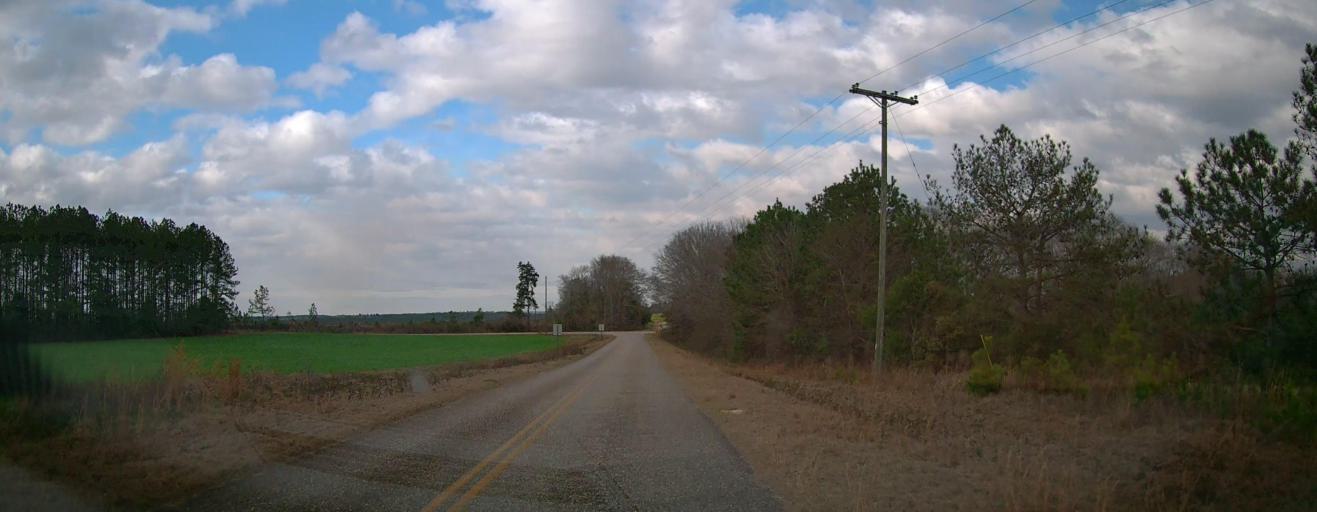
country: US
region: Georgia
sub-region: Marion County
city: Buena Vista
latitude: 32.4341
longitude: -84.4209
